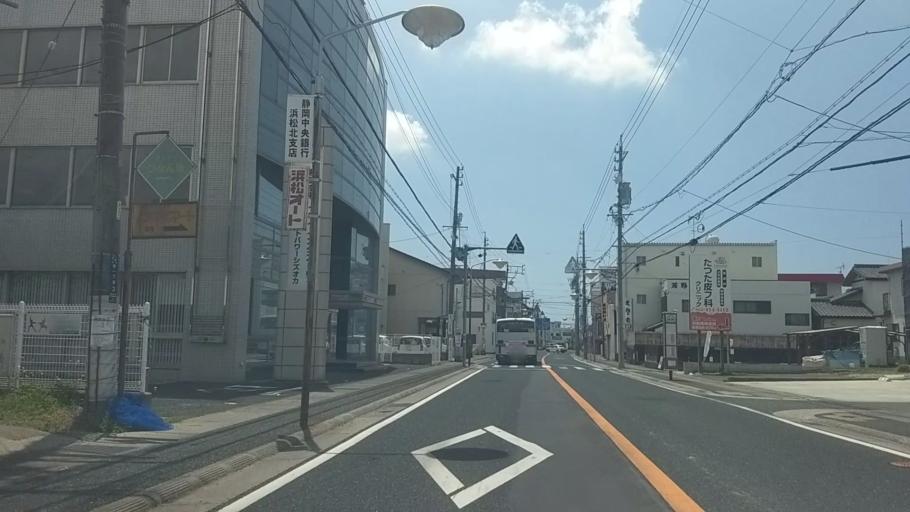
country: JP
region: Shizuoka
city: Hamamatsu
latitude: 34.7373
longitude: 137.7238
